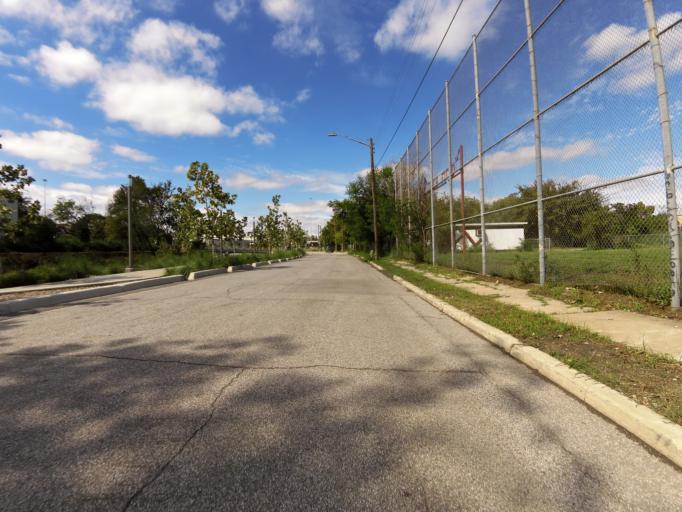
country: US
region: Texas
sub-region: Bexar County
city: San Antonio
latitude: 29.4303
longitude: -98.4965
